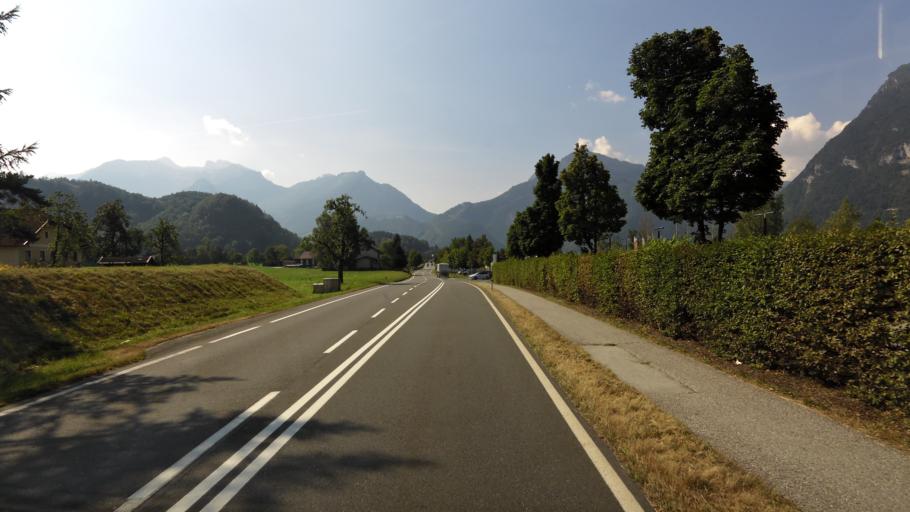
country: AT
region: Salzburg
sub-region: Politischer Bezirk Hallein
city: Golling an der Salzach
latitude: 47.6096
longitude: 13.1676
